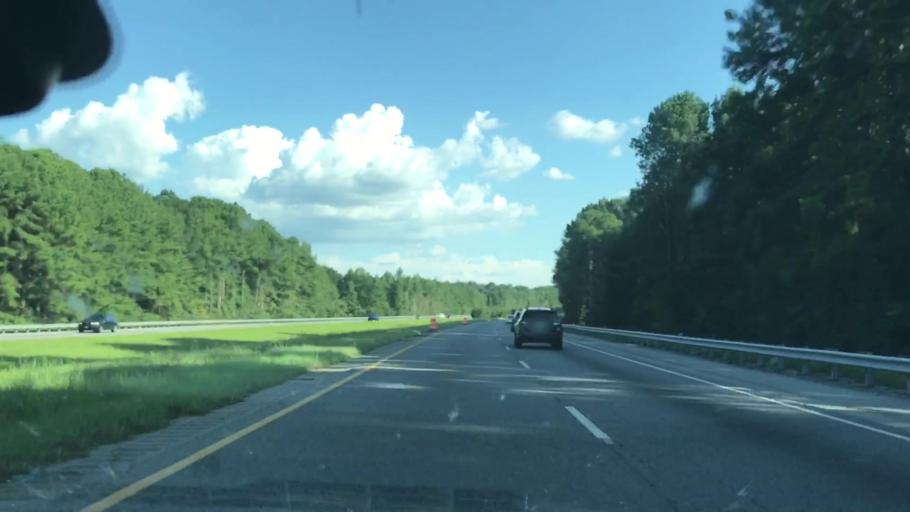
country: US
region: Alabama
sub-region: Russell County
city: Phenix City
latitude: 32.6207
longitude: -84.9530
